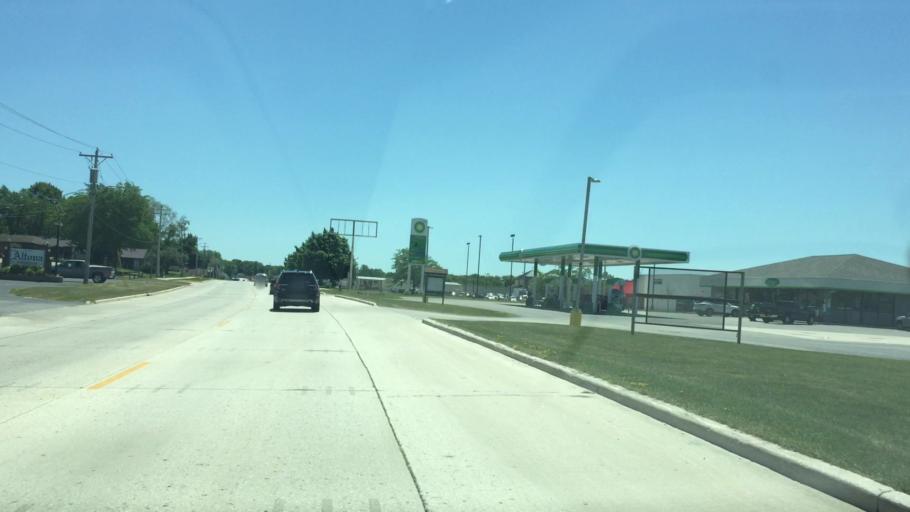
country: US
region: Wisconsin
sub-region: Calumet County
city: New Holstein
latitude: 43.9570
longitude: -88.1085
